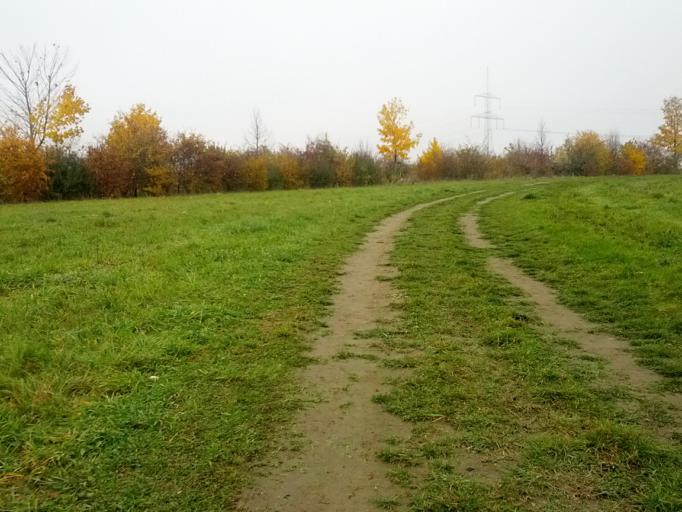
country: DE
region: Thuringia
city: Bischofroda
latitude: 50.9974
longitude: 10.4040
